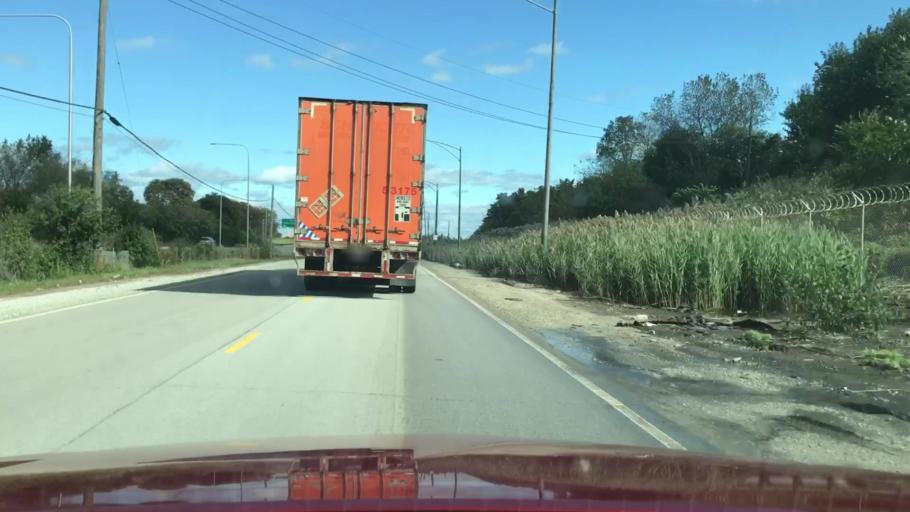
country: US
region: Illinois
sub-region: Cook County
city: Dolton
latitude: 41.7026
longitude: -87.5906
